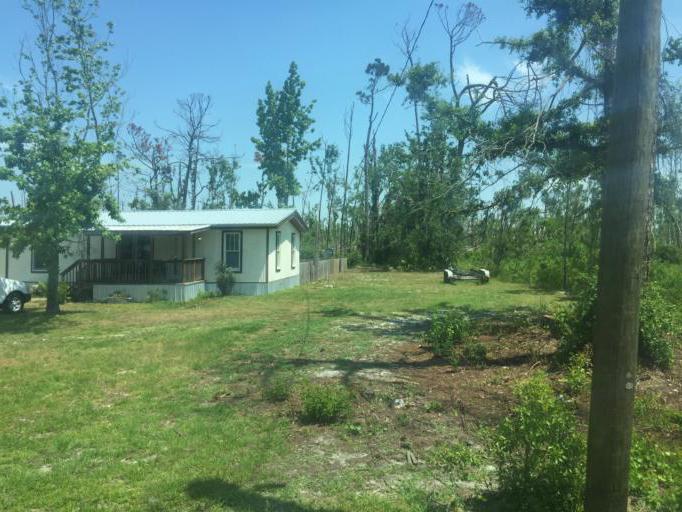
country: US
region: Florida
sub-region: Bay County
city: Hiland Park
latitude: 30.2105
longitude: -85.6312
